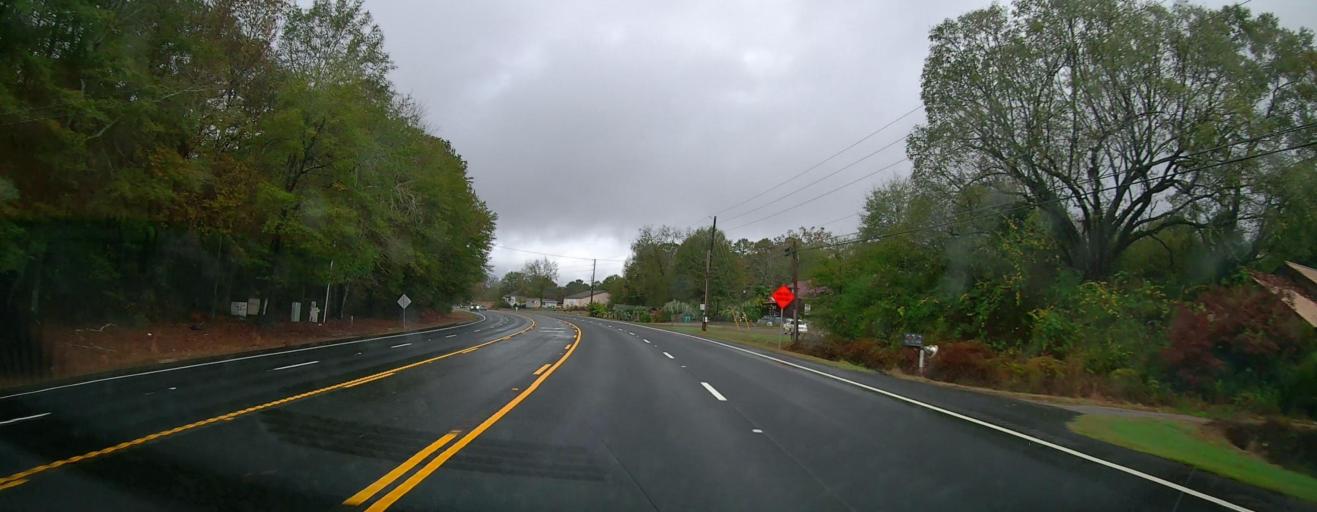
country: US
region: Georgia
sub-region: Clarke County
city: Country Club Estates
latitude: 34.0143
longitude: -83.3880
